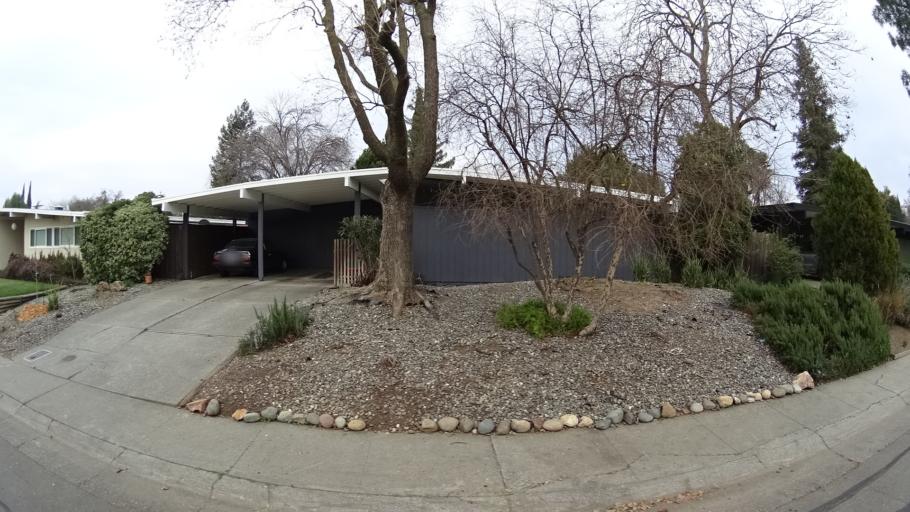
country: US
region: California
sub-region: Yolo County
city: Davis
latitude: 38.5573
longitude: -121.7377
